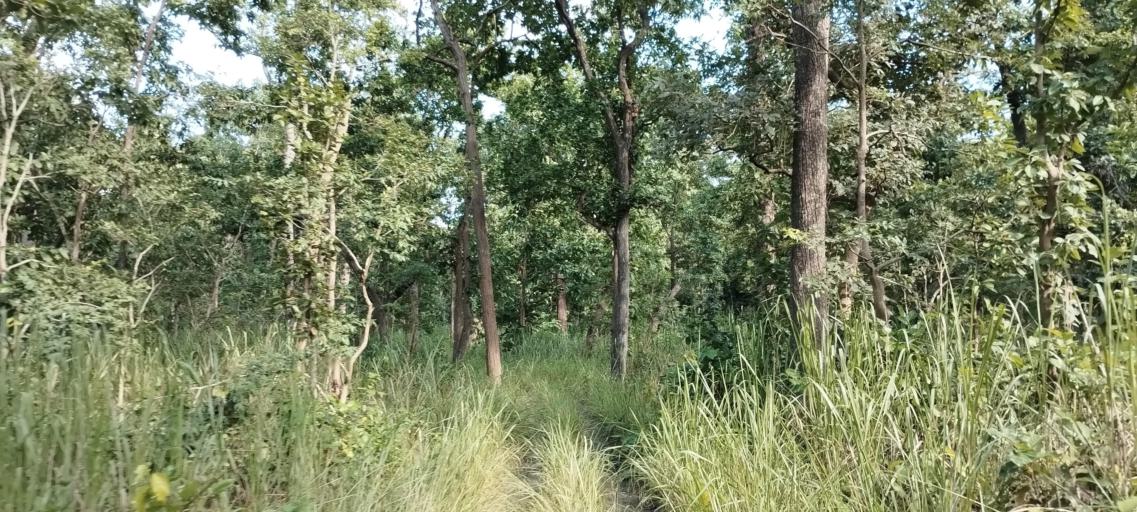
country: NP
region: Far Western
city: Tikapur
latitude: 28.5513
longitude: 81.2838
